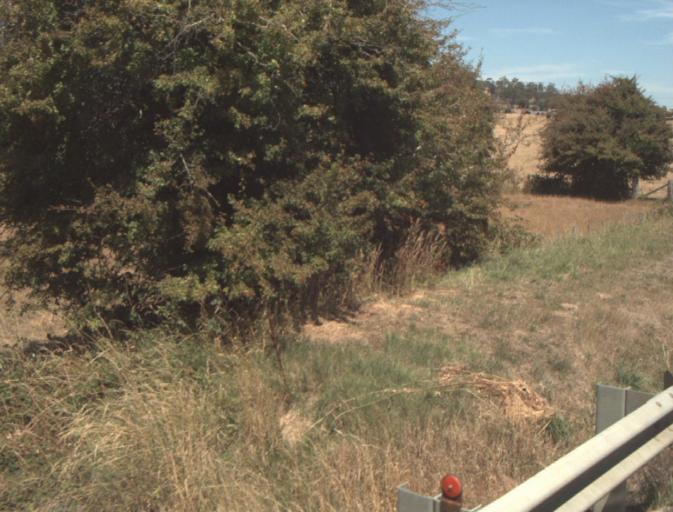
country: AU
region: Tasmania
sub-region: Launceston
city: Mayfield
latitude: -41.3675
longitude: 147.1415
